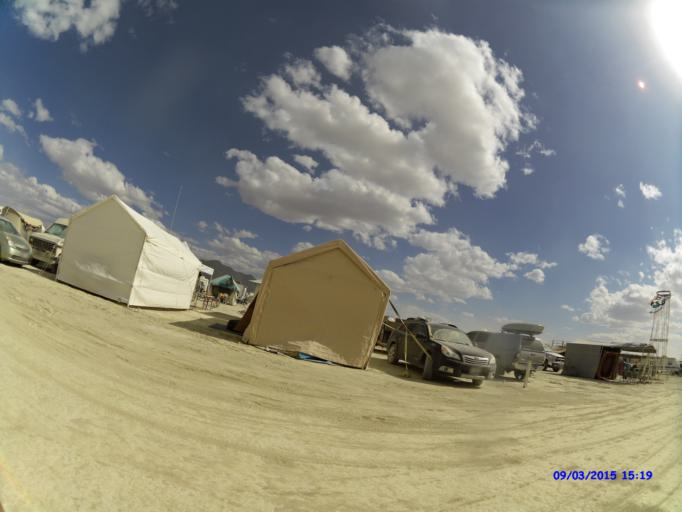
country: US
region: Nevada
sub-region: Pershing County
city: Lovelock
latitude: 40.7797
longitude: -119.1992
